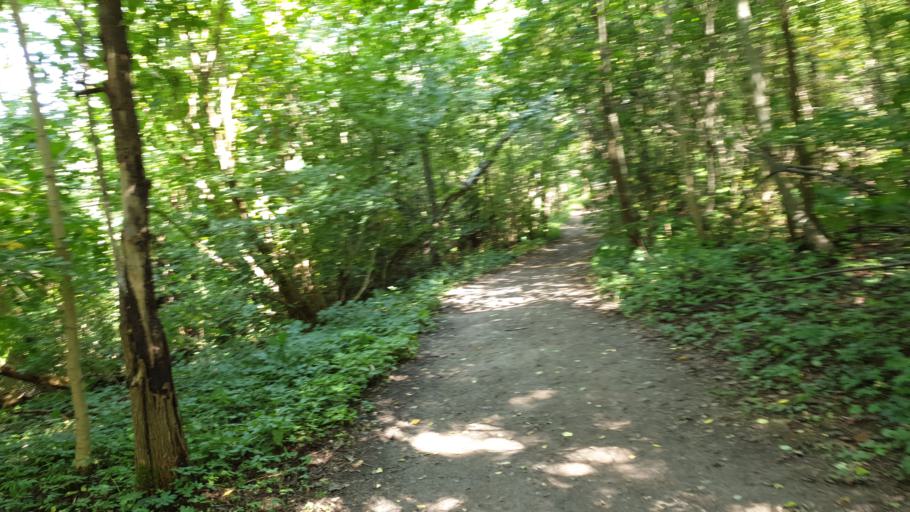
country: LT
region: Vilnius County
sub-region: Vilniaus Rajonas
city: Vievis
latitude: 54.8194
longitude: 24.9368
